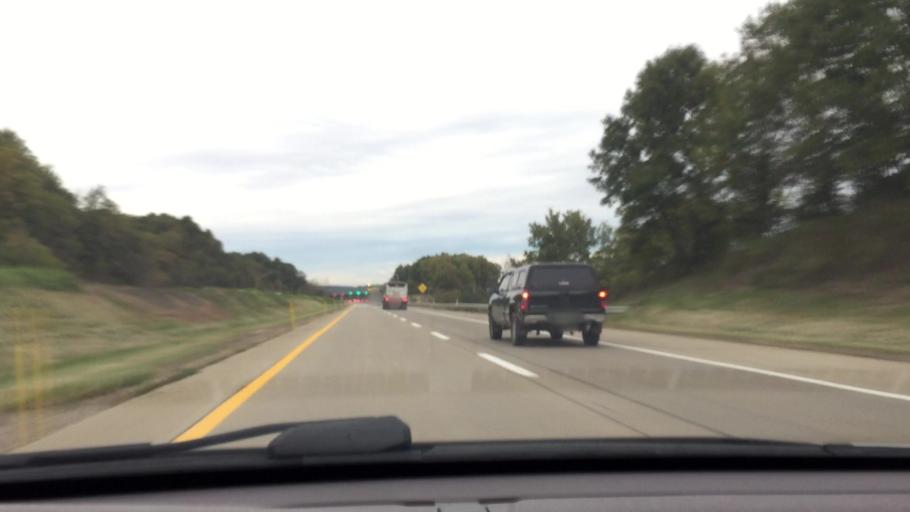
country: US
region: Pennsylvania
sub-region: Lawrence County
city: Oakland
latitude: 40.9388
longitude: -80.3914
